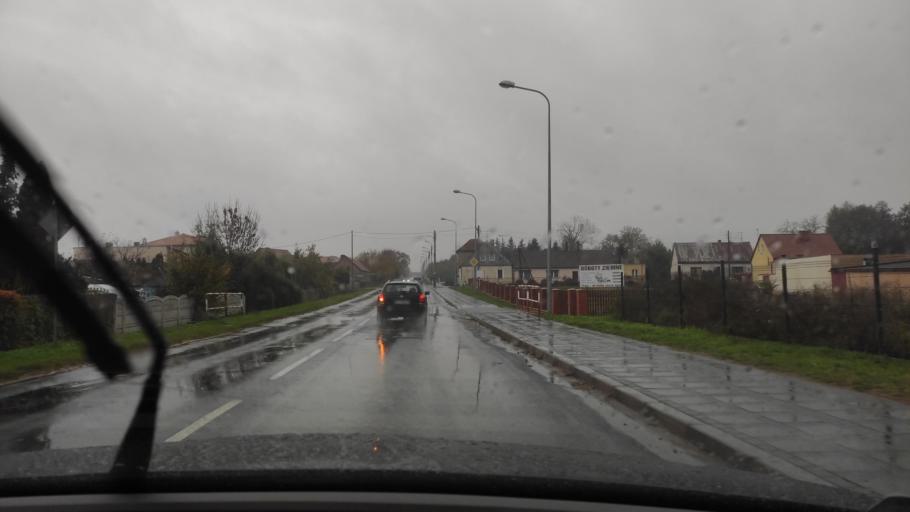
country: PL
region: Greater Poland Voivodeship
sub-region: Powiat poznanski
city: Kornik
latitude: 52.2295
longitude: 17.0939
